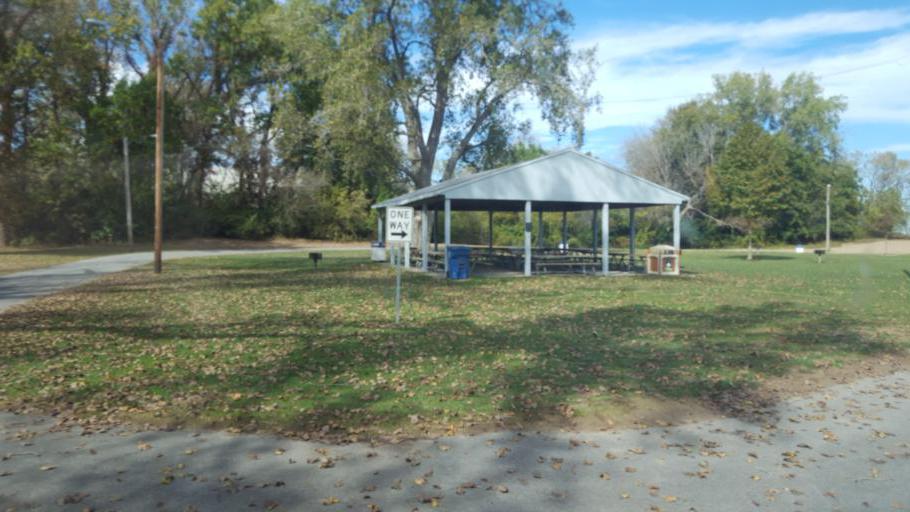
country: US
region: Ohio
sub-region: Erie County
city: Huron
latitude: 41.3950
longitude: -82.5451
